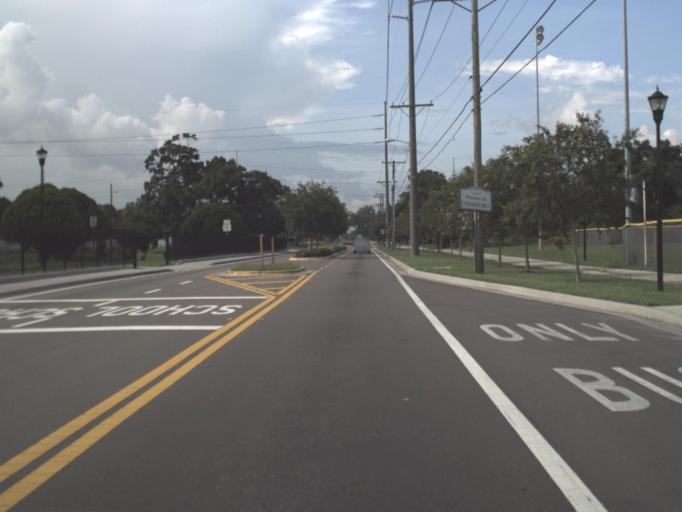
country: US
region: Florida
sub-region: Hillsborough County
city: Tampa
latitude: 27.9810
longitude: -82.4348
